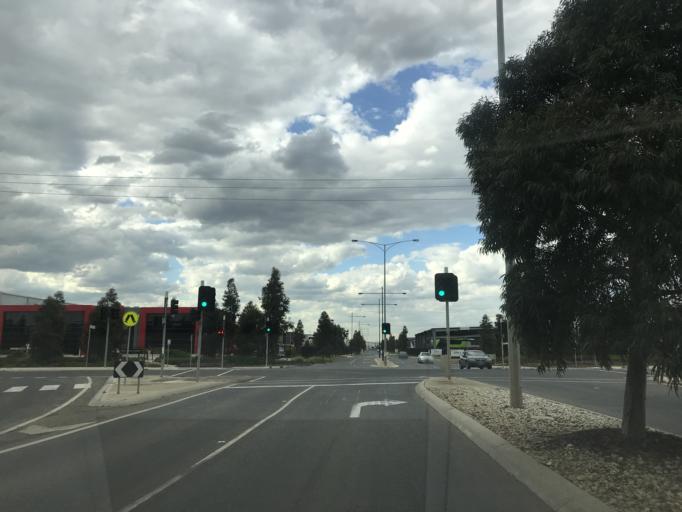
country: AU
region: Victoria
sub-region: Wyndham
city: Truganina
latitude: -37.8098
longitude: 144.7394
